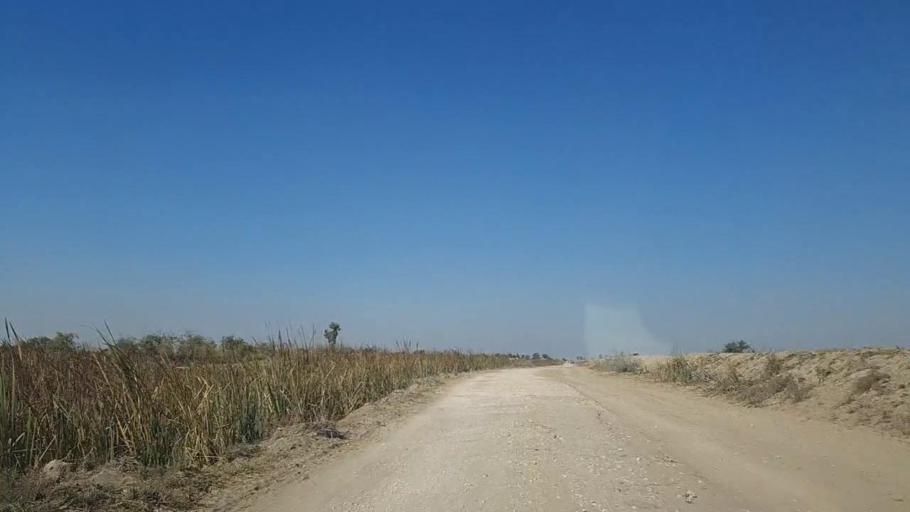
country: PK
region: Sindh
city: Sanghar
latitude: 26.2135
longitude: 68.9292
